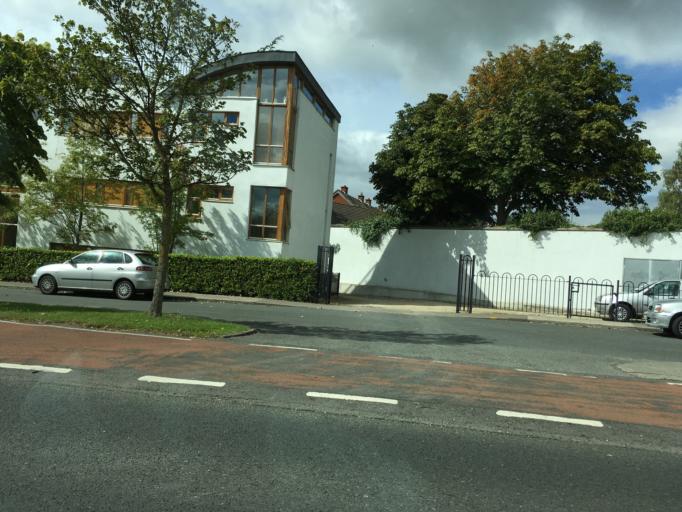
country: IE
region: Leinster
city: Little Bray
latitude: 53.1904
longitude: -6.1248
